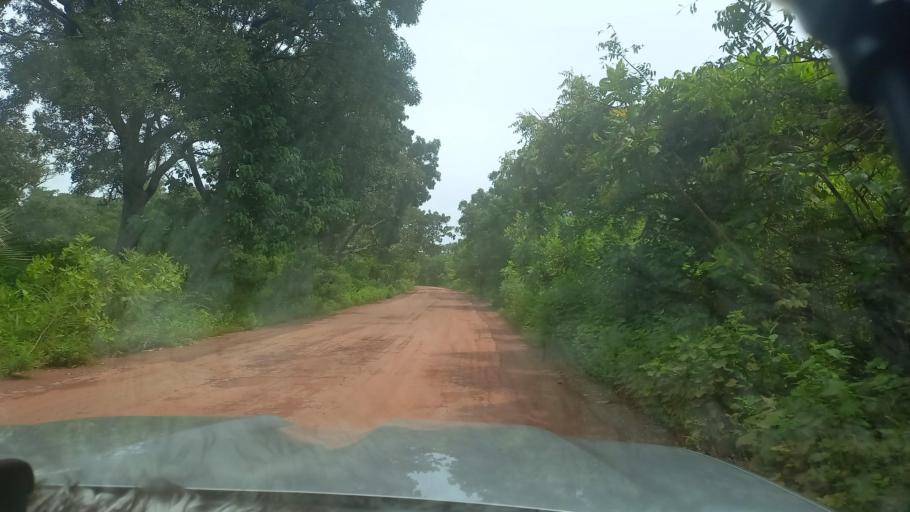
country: SN
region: Kolda
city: Marsassoum
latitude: 12.9053
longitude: -16.0168
